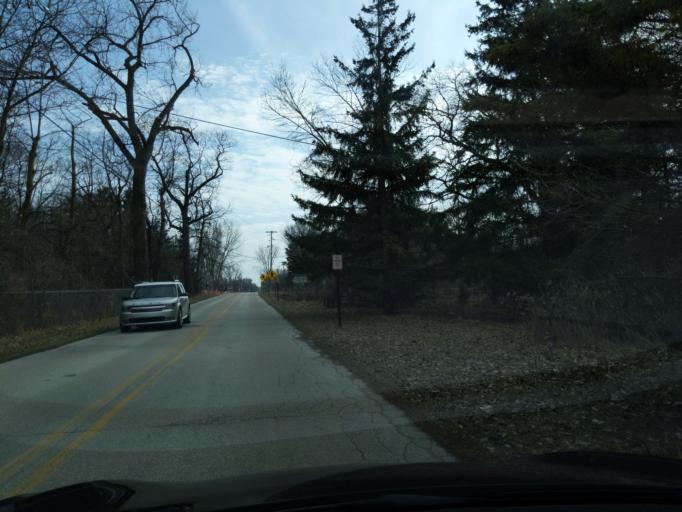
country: US
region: Michigan
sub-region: Bay County
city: Bay City
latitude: 43.6709
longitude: -83.9123
